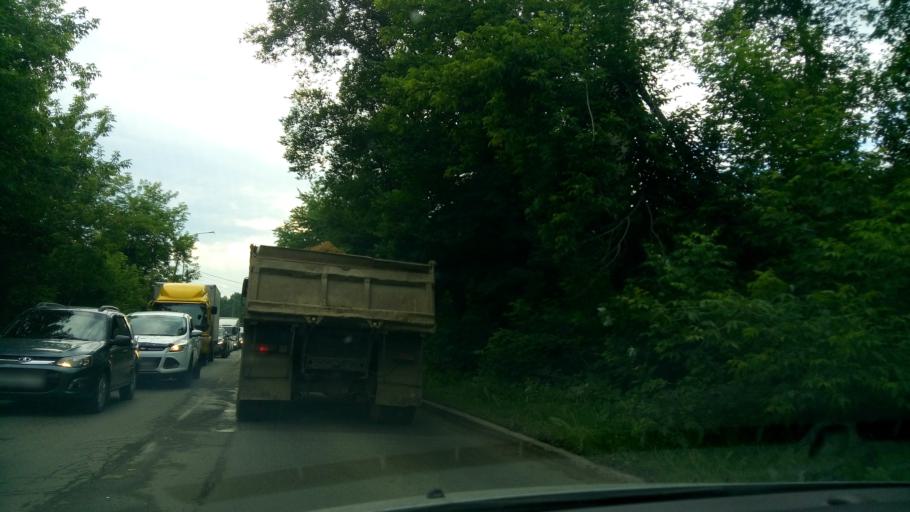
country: RU
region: Sverdlovsk
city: Yekaterinburg
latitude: 56.8819
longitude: 60.6928
